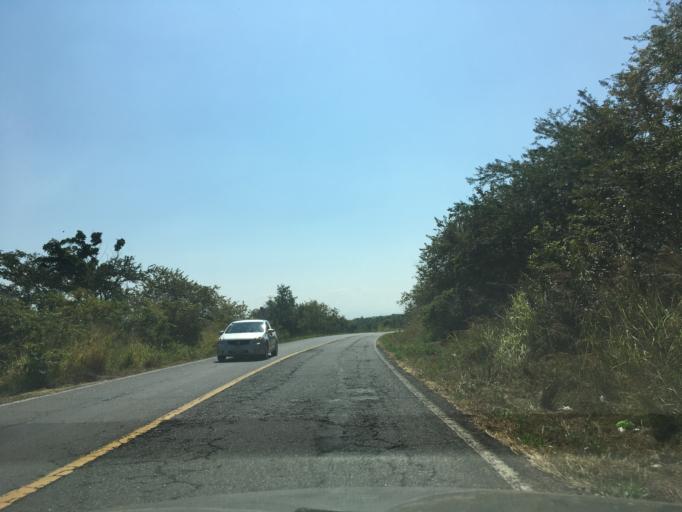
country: MX
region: Michoacan
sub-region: Gabriel Zamora
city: Lombardia
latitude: 19.2370
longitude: -102.0499
